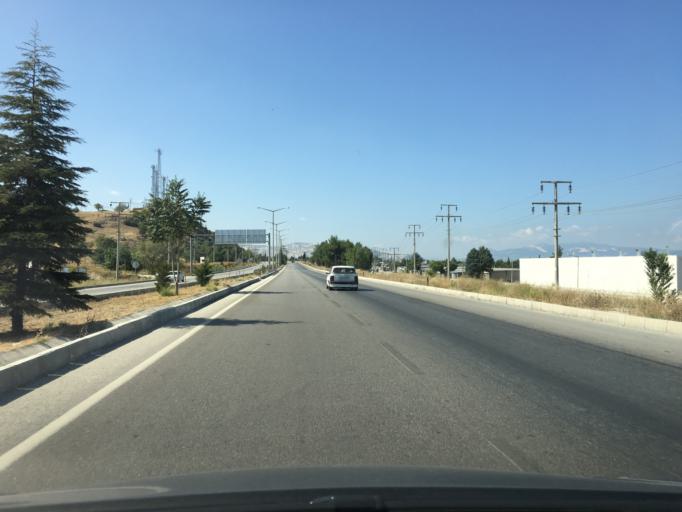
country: TR
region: Burdur
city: Burdur
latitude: 37.7469
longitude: 30.3200
